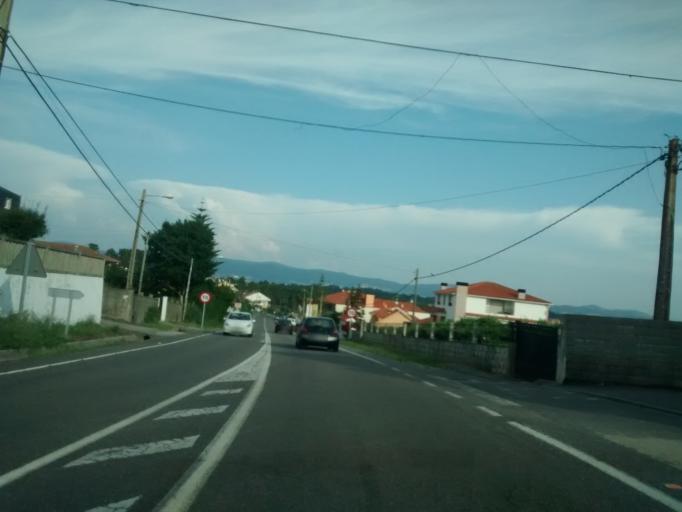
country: ES
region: Galicia
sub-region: Provincia de Pontevedra
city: Sanxenxo
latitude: 42.4043
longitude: -8.8523
